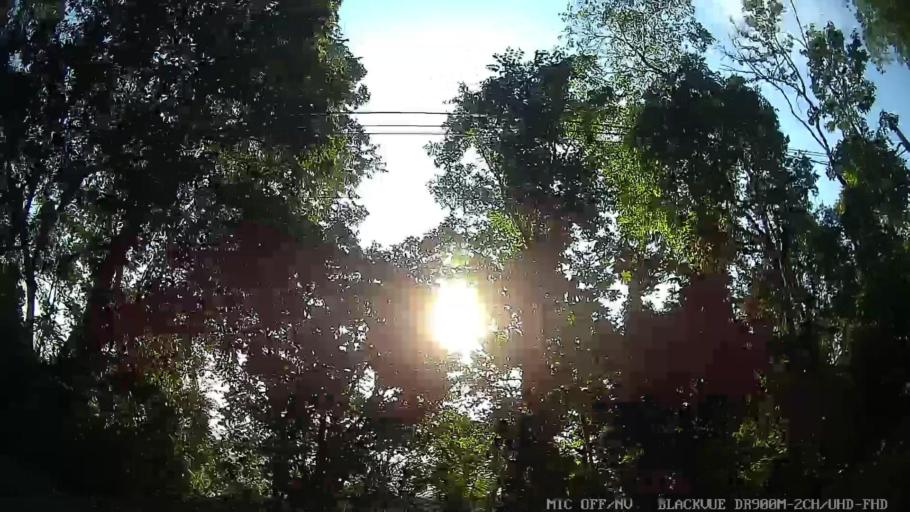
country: BR
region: Sao Paulo
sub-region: Guaruja
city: Guaruja
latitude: -23.9834
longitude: -46.2590
